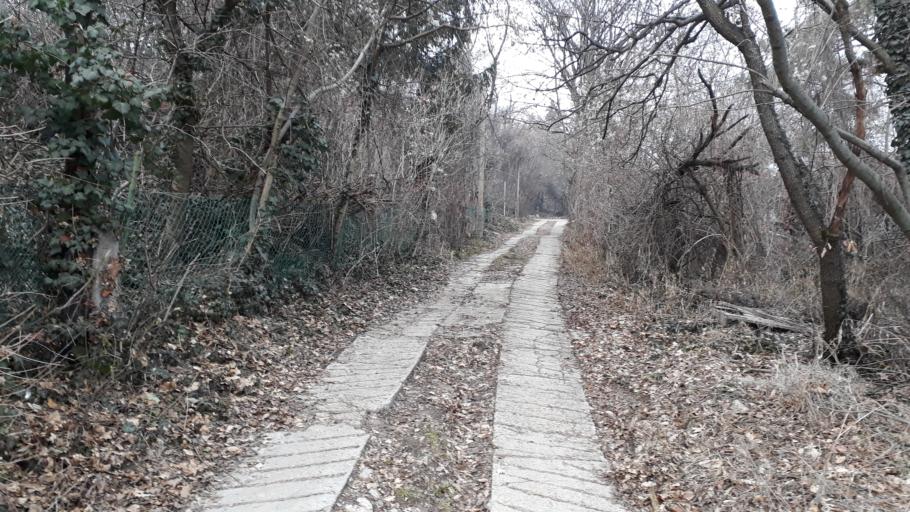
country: HU
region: Pest
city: Budaors
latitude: 47.4850
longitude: 18.9708
